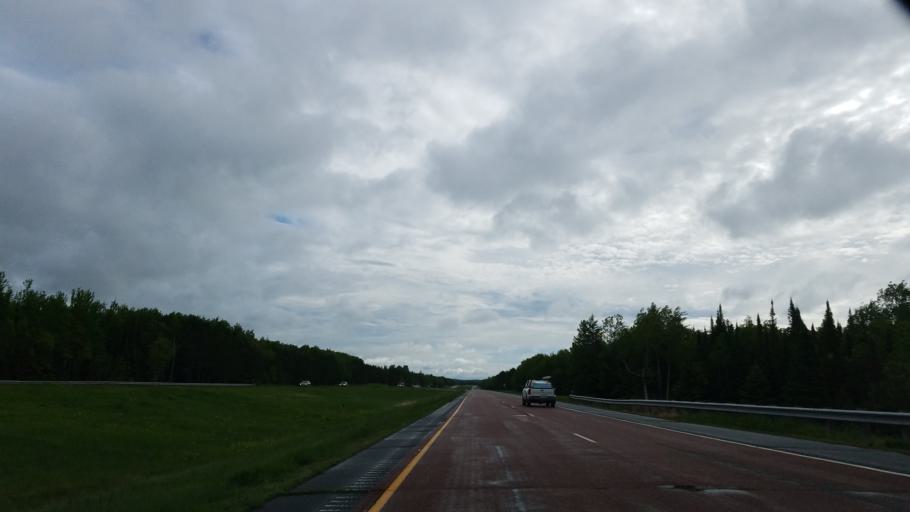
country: US
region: Minnesota
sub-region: Saint Louis County
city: Arnold
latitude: 46.9114
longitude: -91.8832
